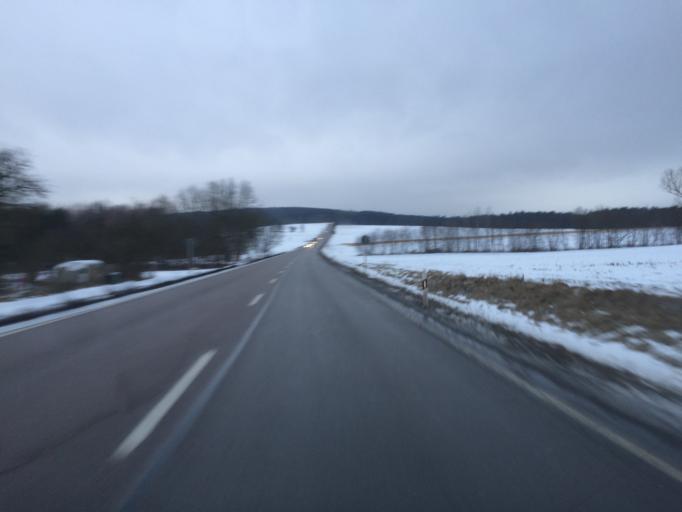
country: DE
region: Bavaria
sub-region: Upper Palatinate
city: Breitenbrunn
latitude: 49.3530
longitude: 12.0644
